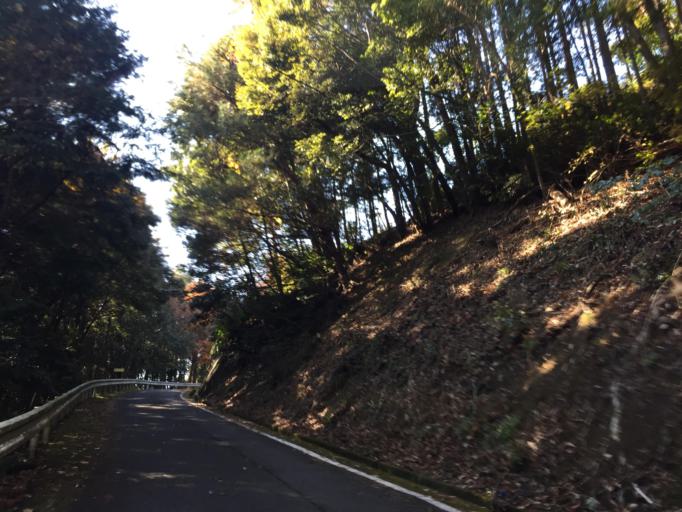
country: JP
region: Wakayama
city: Iwade
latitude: 34.1449
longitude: 135.4094
